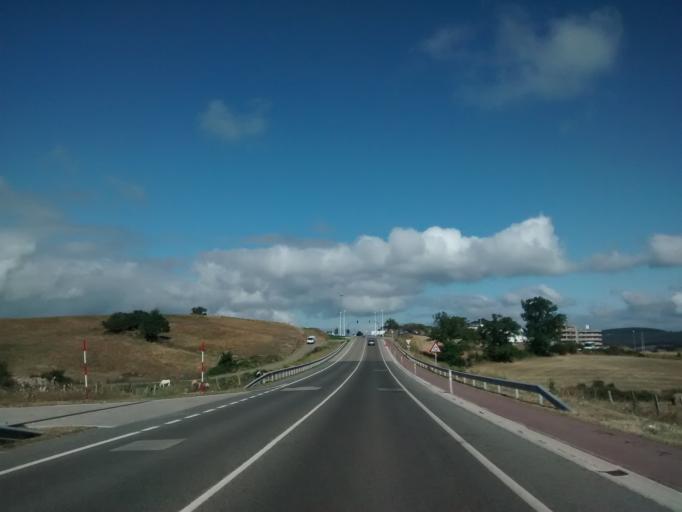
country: ES
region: Cantabria
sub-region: Provincia de Cantabria
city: Reinosa
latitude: 43.0070
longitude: -4.1365
